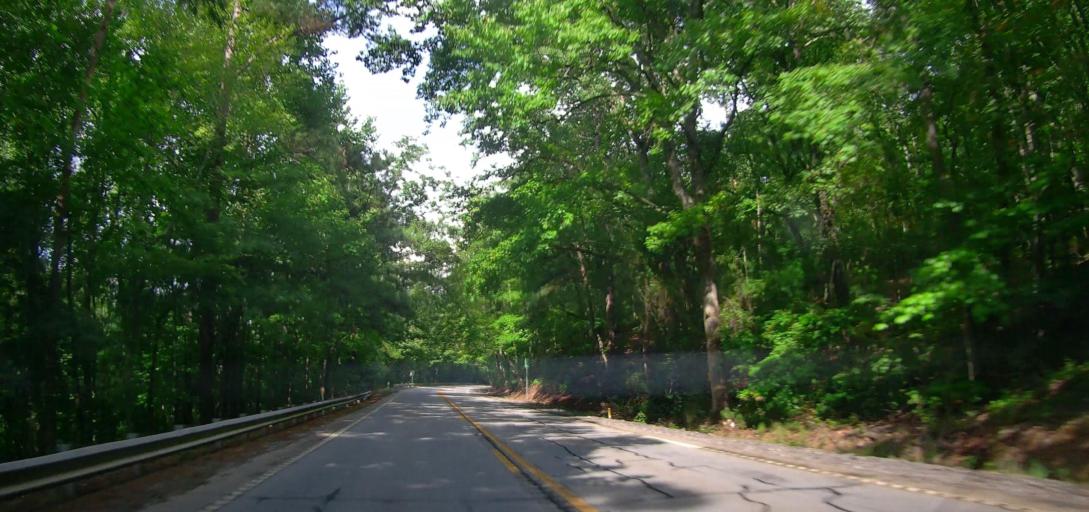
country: US
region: Georgia
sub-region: Harris County
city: Pine Mountain
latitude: 32.8185
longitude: -84.8486
